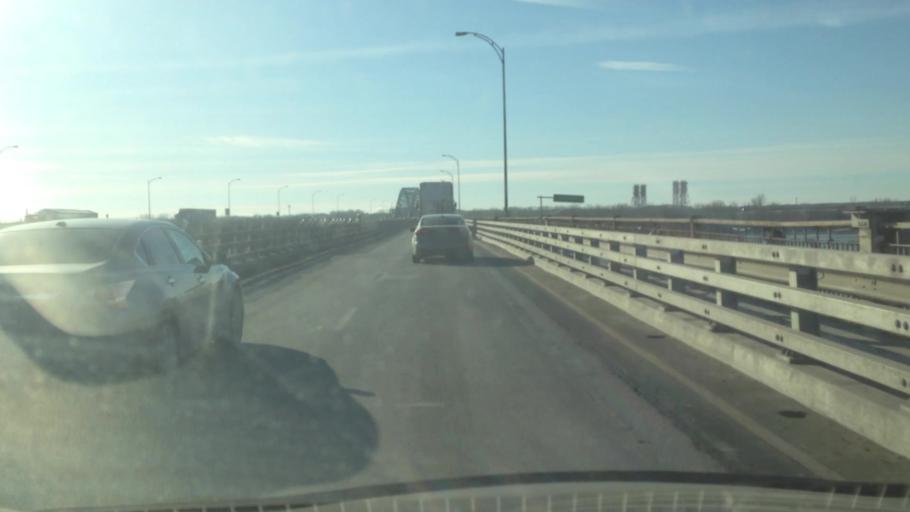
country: CA
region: Quebec
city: Montreal-Ouest
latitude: 45.4210
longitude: -73.6528
